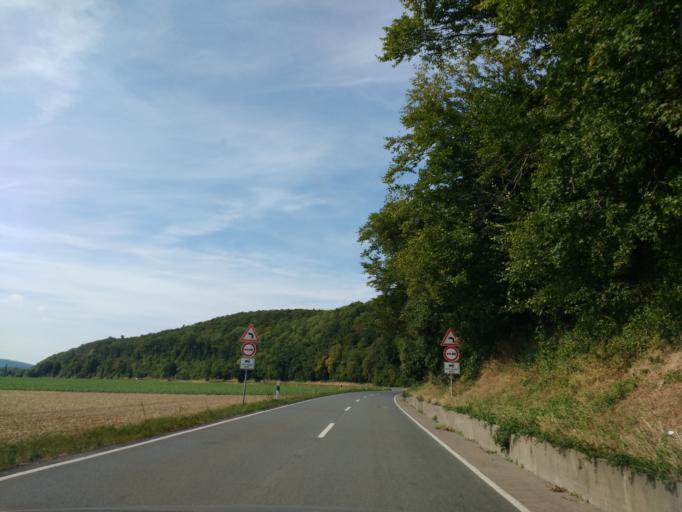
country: DE
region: Lower Saxony
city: Hehlen
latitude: 52.0407
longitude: 9.4203
